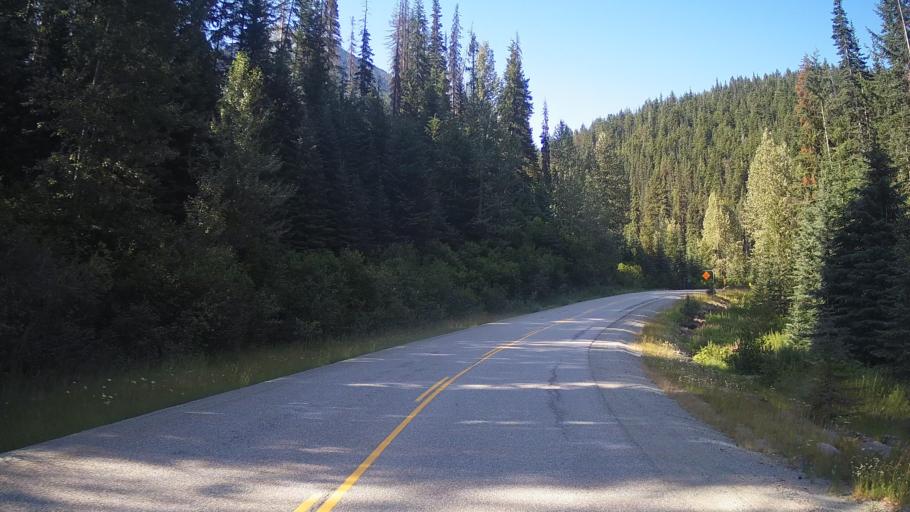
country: CA
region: British Columbia
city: Lillooet
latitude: 50.4333
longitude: -122.2536
